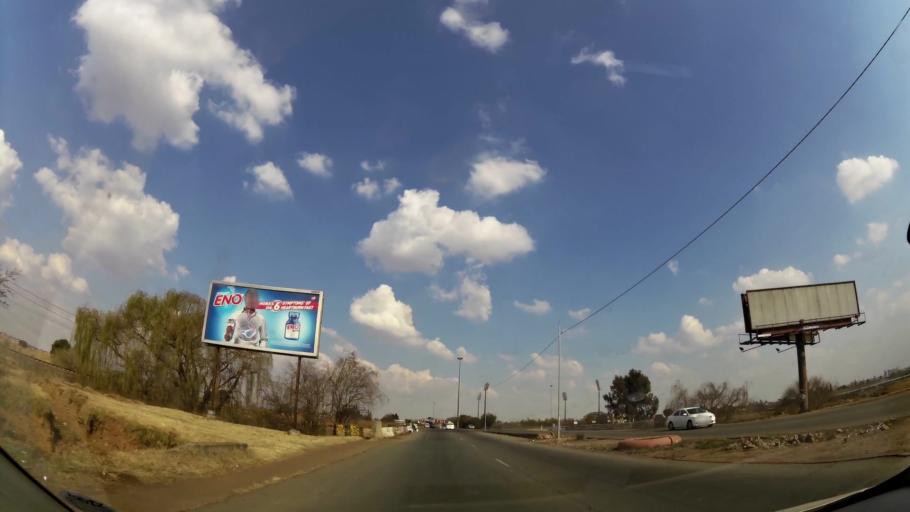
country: ZA
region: Gauteng
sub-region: Ekurhuleni Metropolitan Municipality
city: Germiston
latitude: -26.2998
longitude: 28.1600
